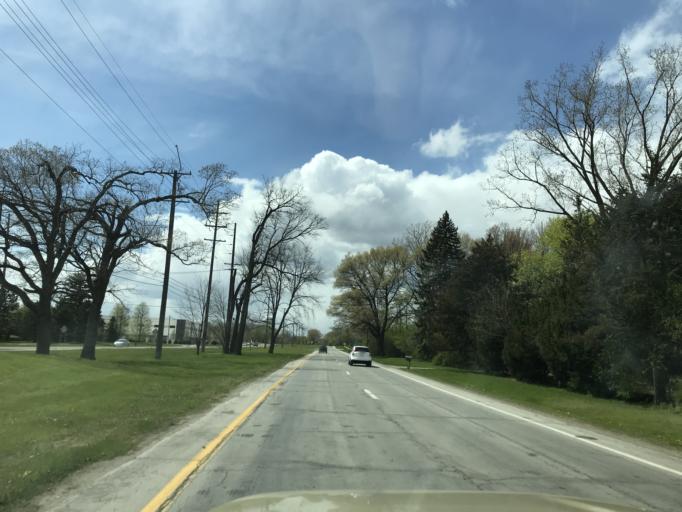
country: US
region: Michigan
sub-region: Wayne County
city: Plymouth
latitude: 42.3837
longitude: -83.4399
